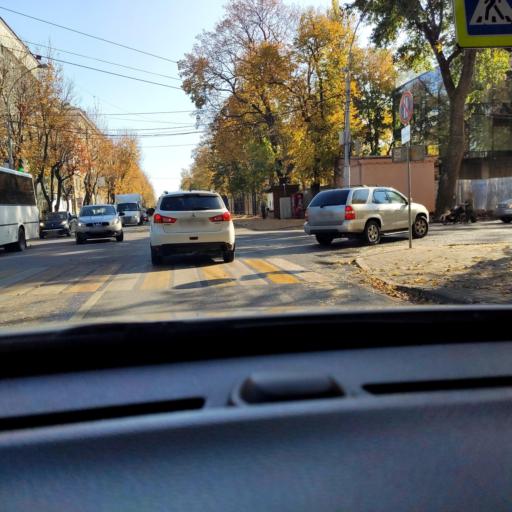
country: RU
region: Voronezj
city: Voronezh
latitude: 51.6765
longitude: 39.2048
